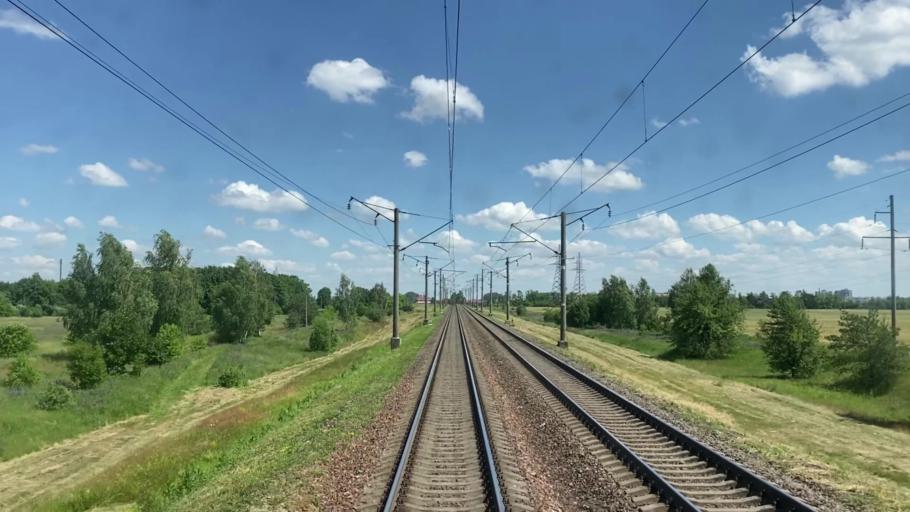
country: BY
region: Brest
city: Baranovichi
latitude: 53.0998
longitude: 25.9479
